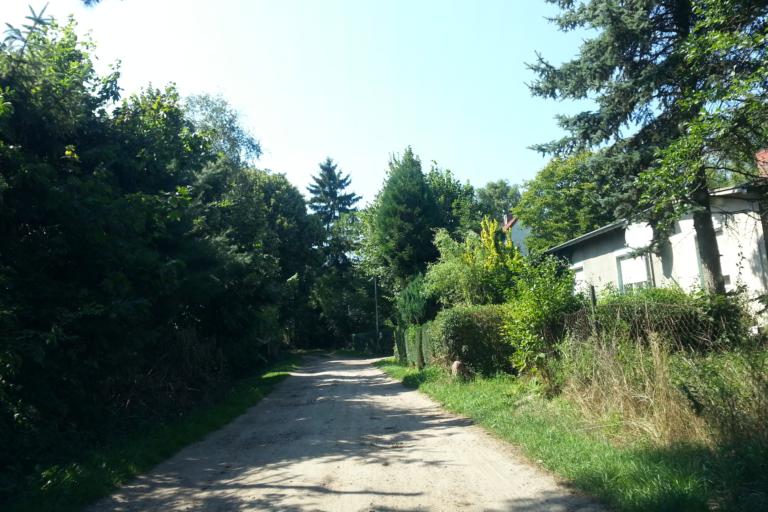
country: DE
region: Mecklenburg-Vorpommern
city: Ducherow
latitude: 53.7003
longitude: 13.8034
